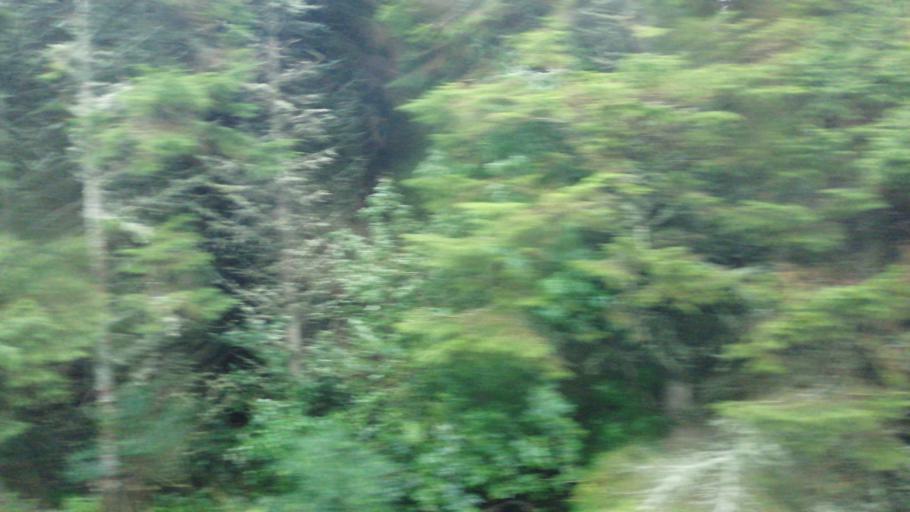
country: GB
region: Scotland
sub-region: Highland
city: Golspie
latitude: 57.9803
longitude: -3.9682
